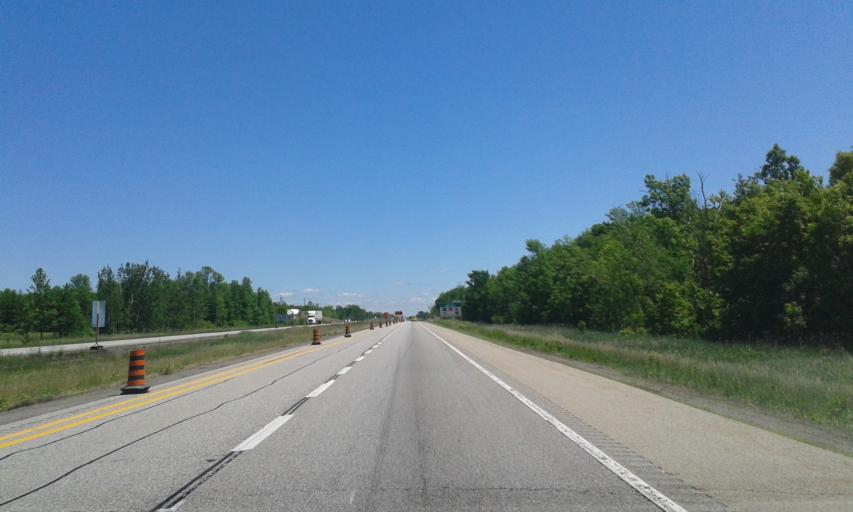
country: US
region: New York
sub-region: St. Lawrence County
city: Ogdensburg
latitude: 44.8671
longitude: -75.3114
